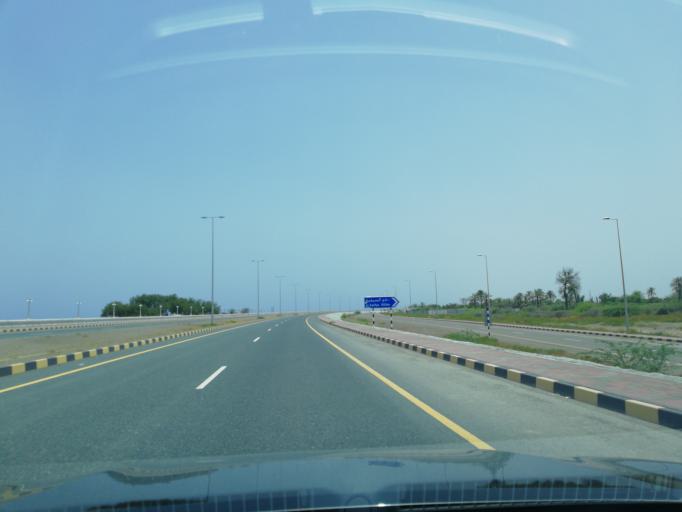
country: OM
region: Al Batinah
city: Shinas
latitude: 24.8280
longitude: 56.4356
